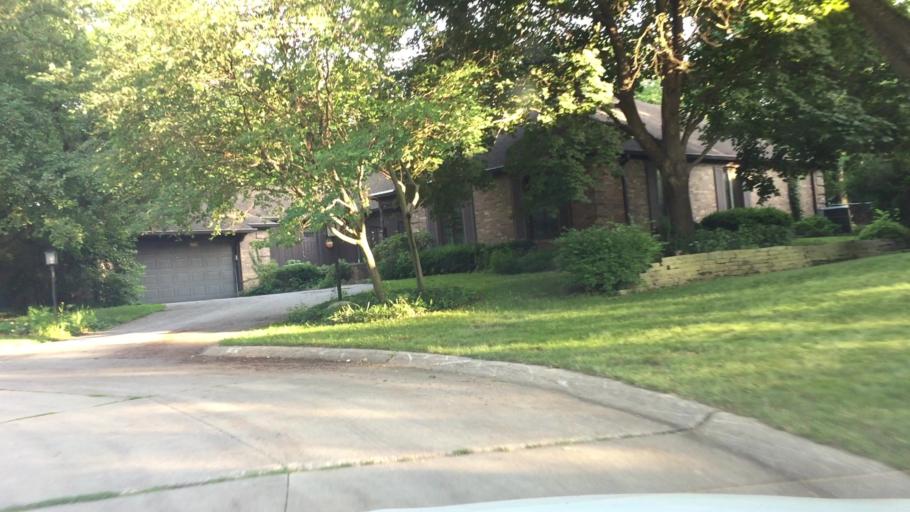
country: US
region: Iowa
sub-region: Johnson County
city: Iowa City
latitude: 41.6609
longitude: -91.5052
